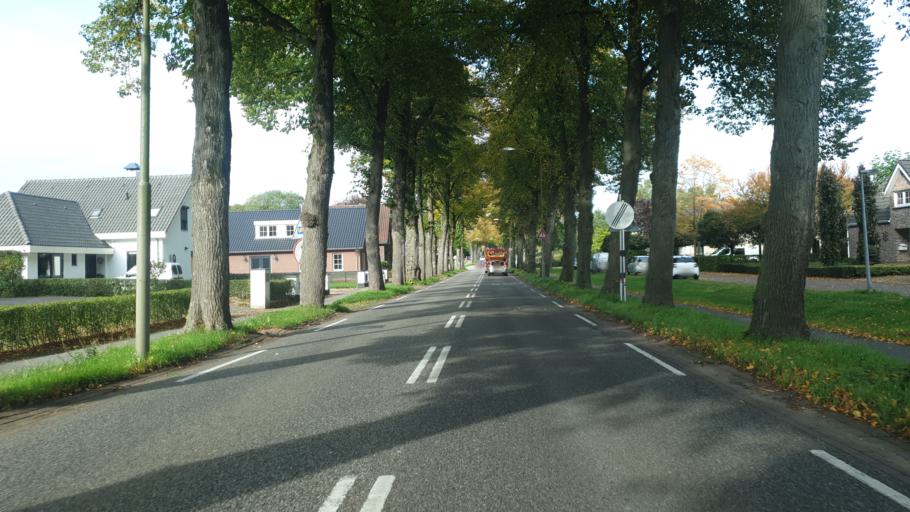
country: NL
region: Gelderland
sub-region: Gemeente Groesbeek
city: Groesbeek
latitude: 51.7851
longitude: 5.9302
